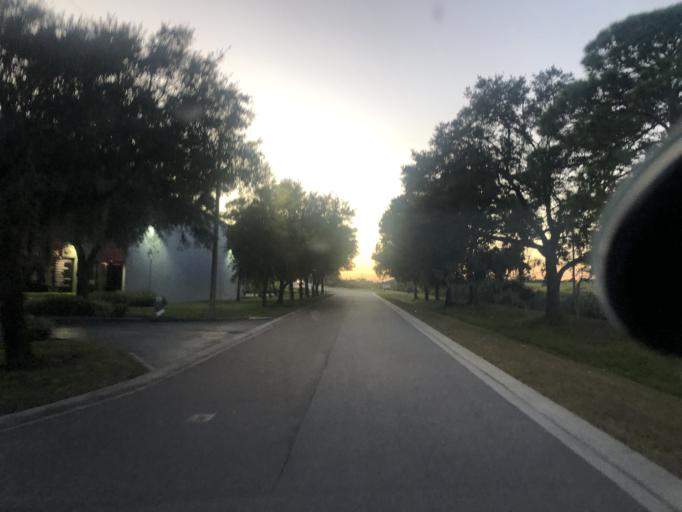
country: US
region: Florida
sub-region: Pinellas County
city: Gandy
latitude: 27.8648
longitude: -82.6576
